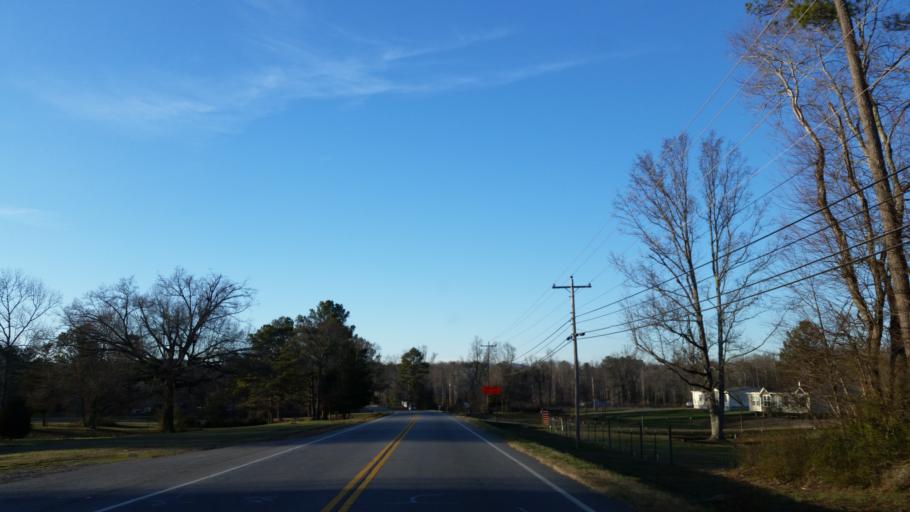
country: US
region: Georgia
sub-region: Whitfield County
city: Dalton
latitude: 34.6452
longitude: -84.9694
